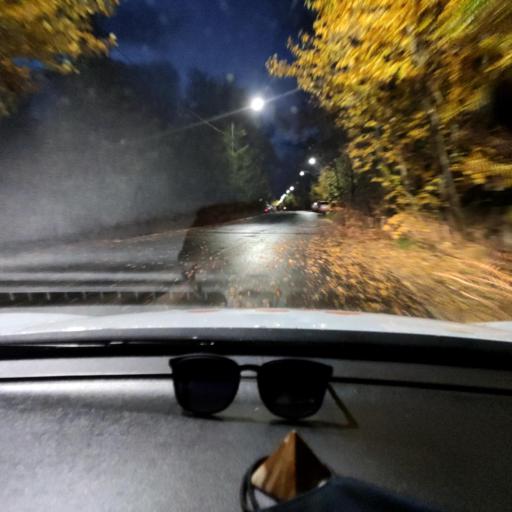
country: RU
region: Tatarstan
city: Verkhniy Uslon
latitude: 55.6042
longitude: 49.0205
